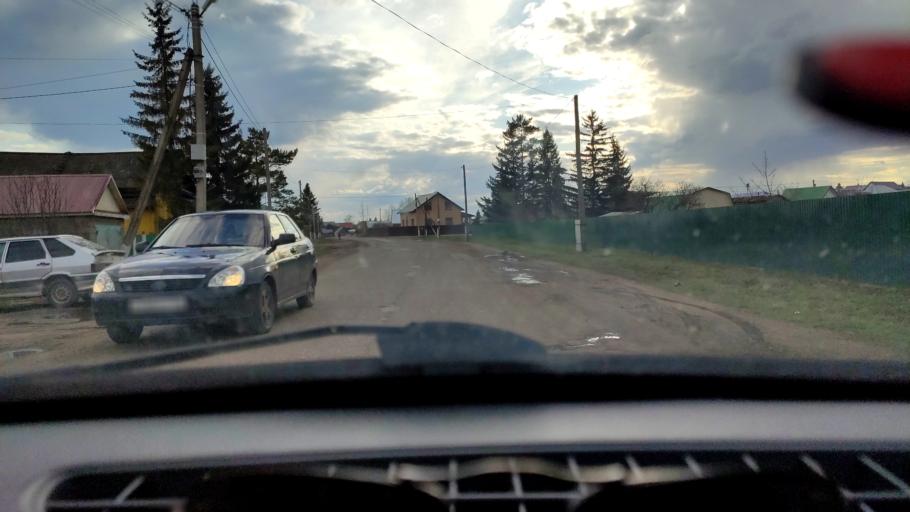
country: RU
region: Bashkortostan
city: Karmaskaly
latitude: 54.3708
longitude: 56.1915
